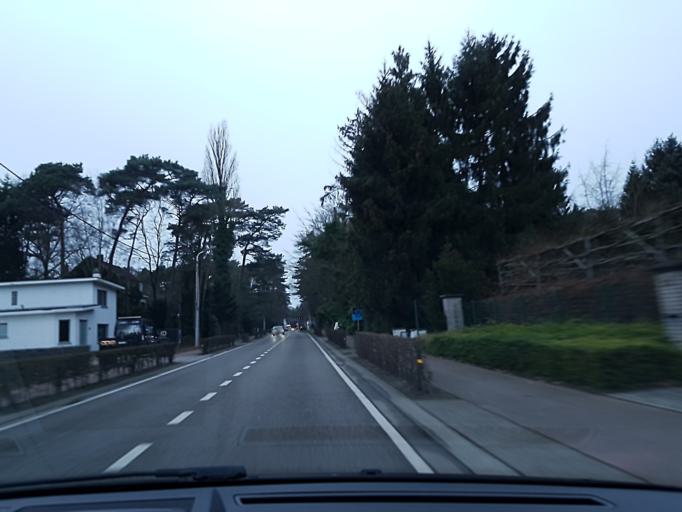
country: BE
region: Flanders
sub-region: Provincie Vlaams-Brabant
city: Keerbergen
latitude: 51.0097
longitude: 4.6027
